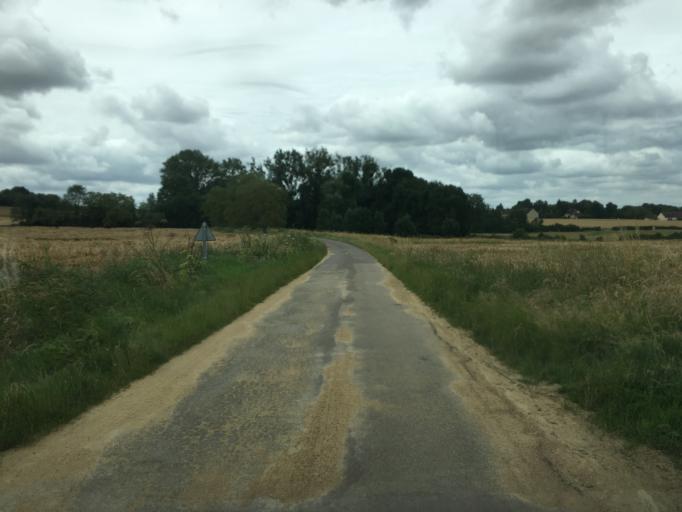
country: FR
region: Bourgogne
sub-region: Departement de l'Yonne
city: Fleury-la-Vallee
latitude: 47.8661
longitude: 3.4148
